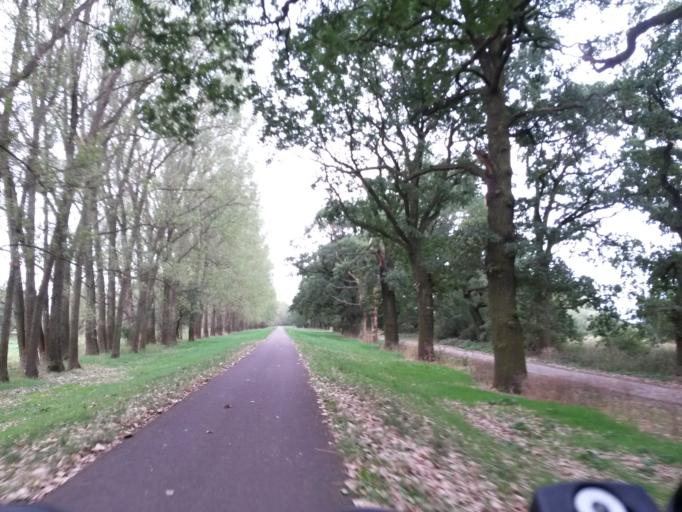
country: DE
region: Saxony-Anhalt
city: Tangermunde
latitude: 52.5311
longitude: 11.9657
